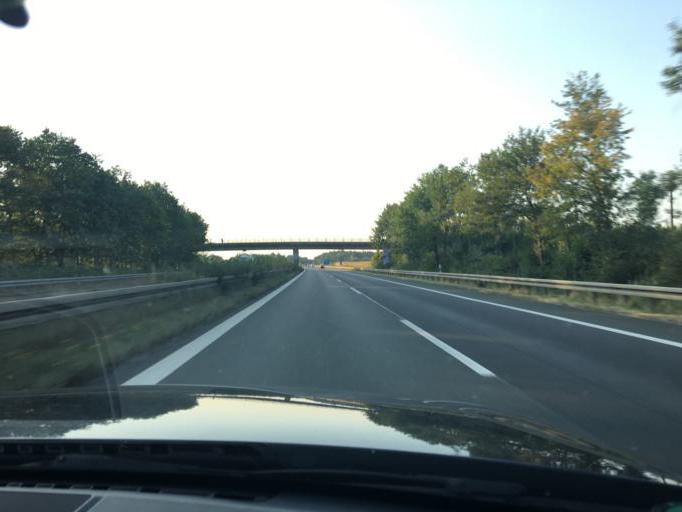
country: DE
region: Bavaria
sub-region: Upper Franconia
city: Buttenheim
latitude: 49.7898
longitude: 11.0322
